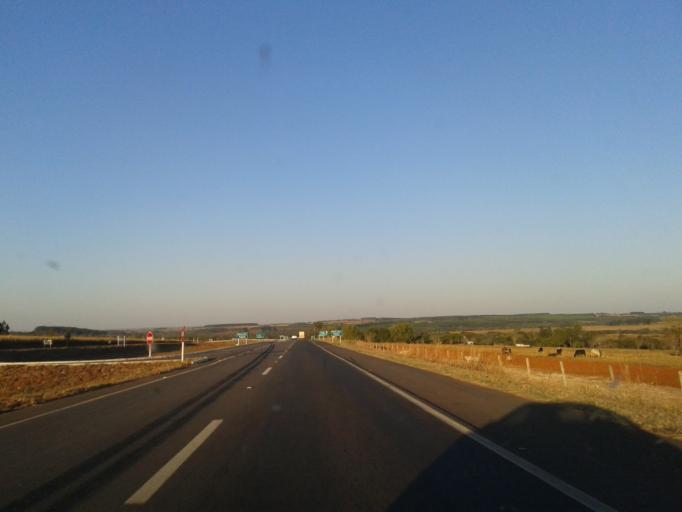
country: BR
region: Goias
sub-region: Goias
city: Goias
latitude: -16.0038
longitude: -50.0270
